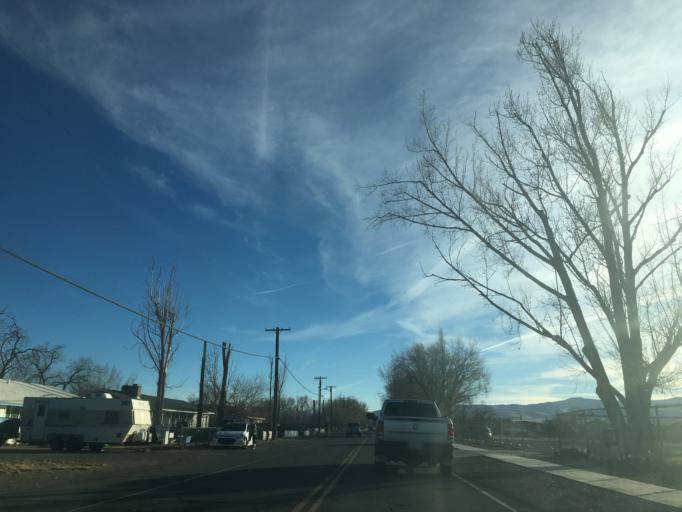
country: US
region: Nevada
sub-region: Lyon County
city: Fernley
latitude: 39.6029
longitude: -119.2465
